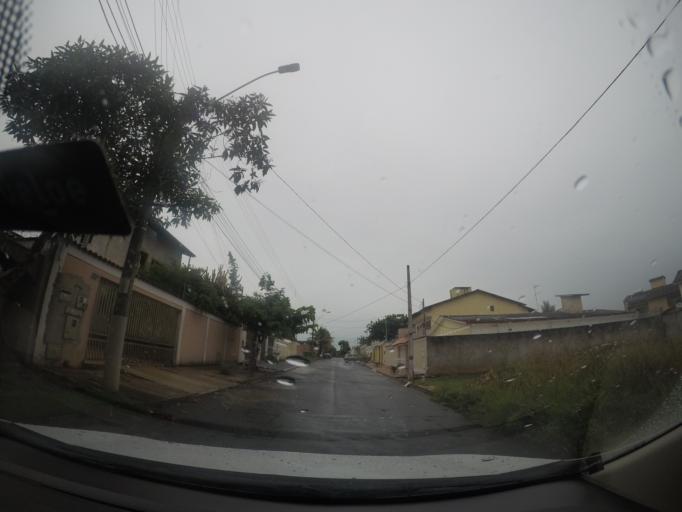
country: BR
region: Goias
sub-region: Goiania
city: Goiania
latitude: -16.6365
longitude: -49.2333
